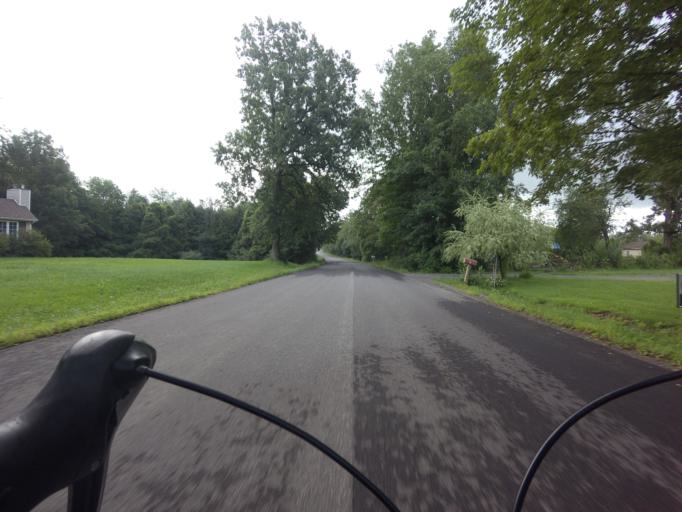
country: CA
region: Ontario
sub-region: Lanark County
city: Smiths Falls
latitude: 44.9561
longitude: -75.7985
